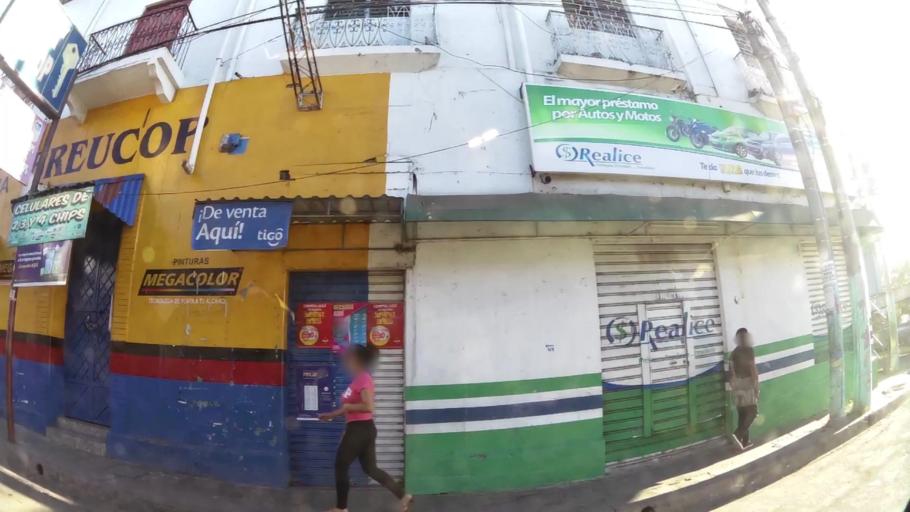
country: SV
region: Sonsonate
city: Sonsonate
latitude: 13.7195
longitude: -89.7264
